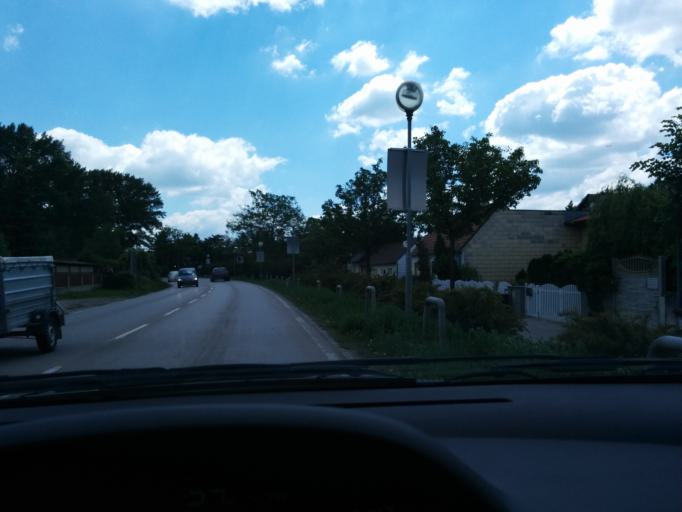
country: AT
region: Lower Austria
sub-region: Politischer Bezirk Baden
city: Oberwaltersdorf
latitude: 47.9848
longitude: 16.2938
